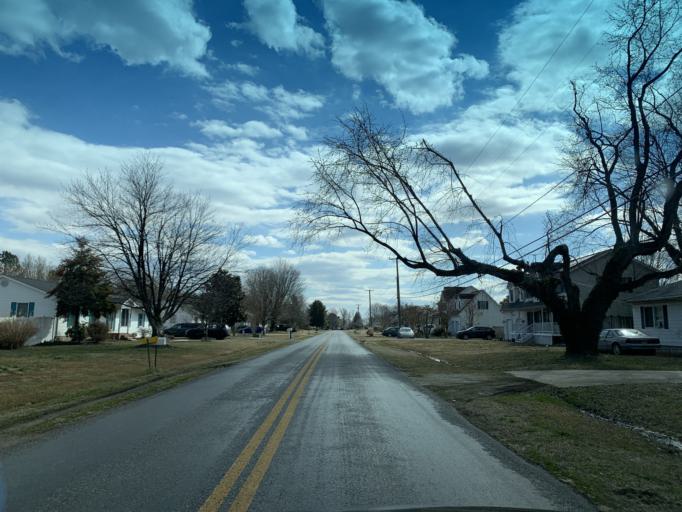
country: US
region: Maryland
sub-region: Queen Anne's County
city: Chester
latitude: 38.9367
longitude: -76.2659
